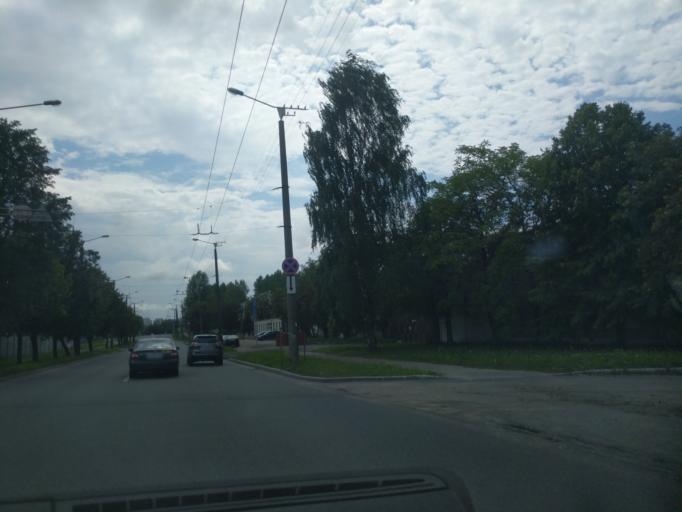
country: BY
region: Minsk
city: Novoye Medvezhino
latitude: 53.8879
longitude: 27.4805
